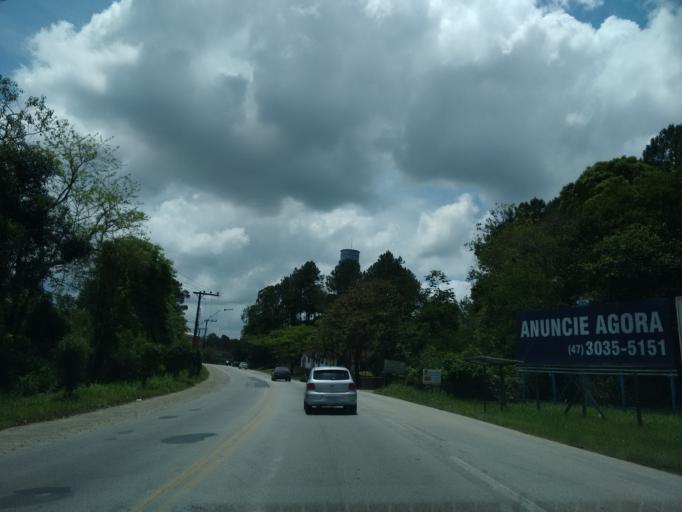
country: BR
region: Santa Catarina
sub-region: Blumenau
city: Blumenau
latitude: -26.9044
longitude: -49.0153
